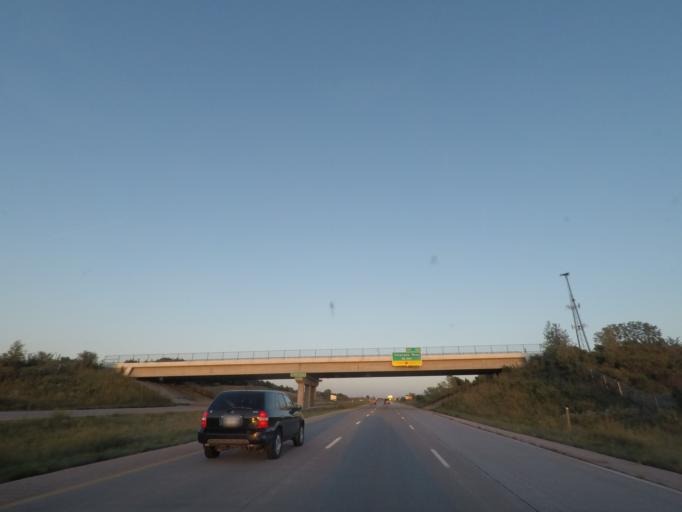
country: US
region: Iowa
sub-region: Polk County
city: West Des Moines
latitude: 41.5223
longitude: -93.7381
